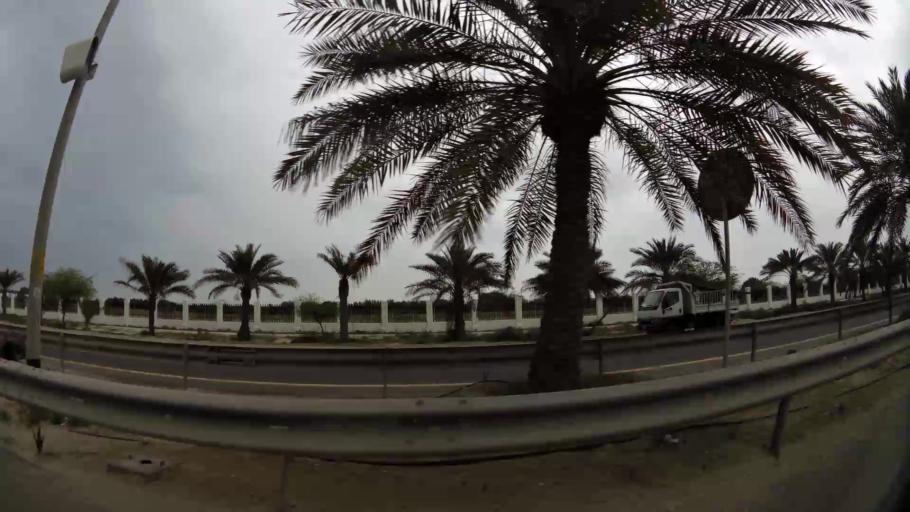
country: BH
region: Central Governorate
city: Dar Kulayb
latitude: 26.0653
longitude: 50.5227
